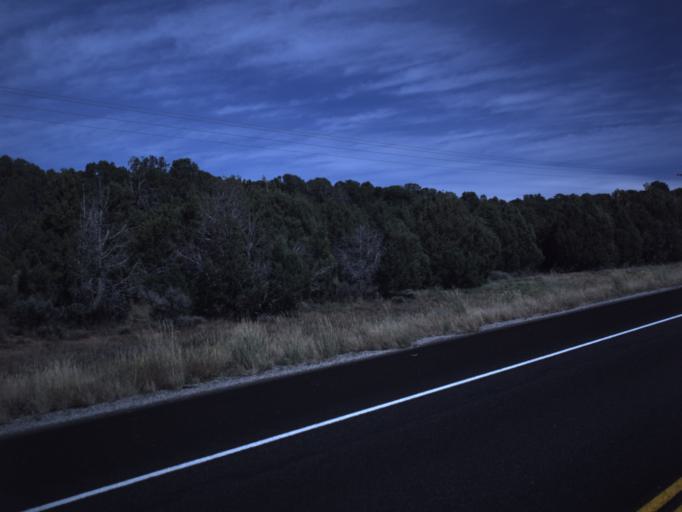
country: US
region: Utah
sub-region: San Juan County
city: Monticello
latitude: 37.8728
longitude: -109.2981
